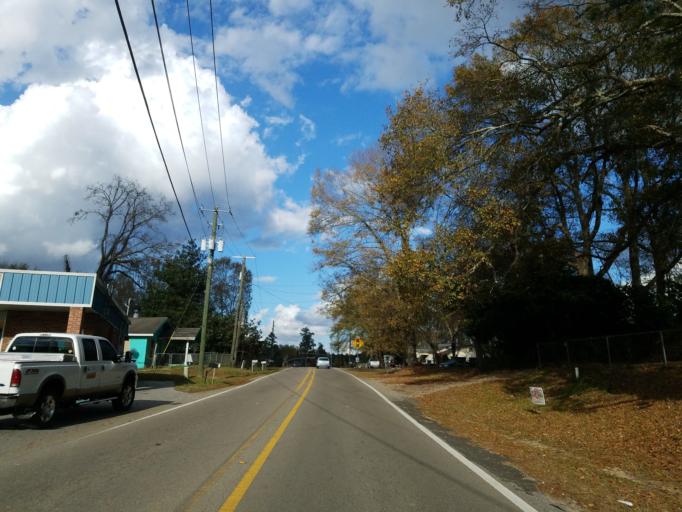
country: US
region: Mississippi
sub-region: Forrest County
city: Glendale
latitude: 31.3597
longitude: -89.3003
